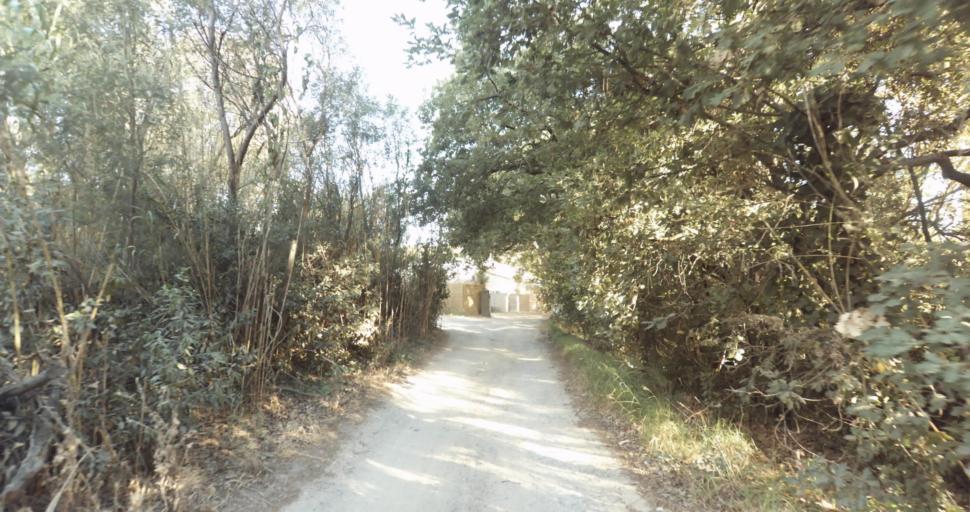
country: FR
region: Provence-Alpes-Cote d'Azur
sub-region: Departement du Var
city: Saint-Tropez
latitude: 43.2559
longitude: 6.6354
